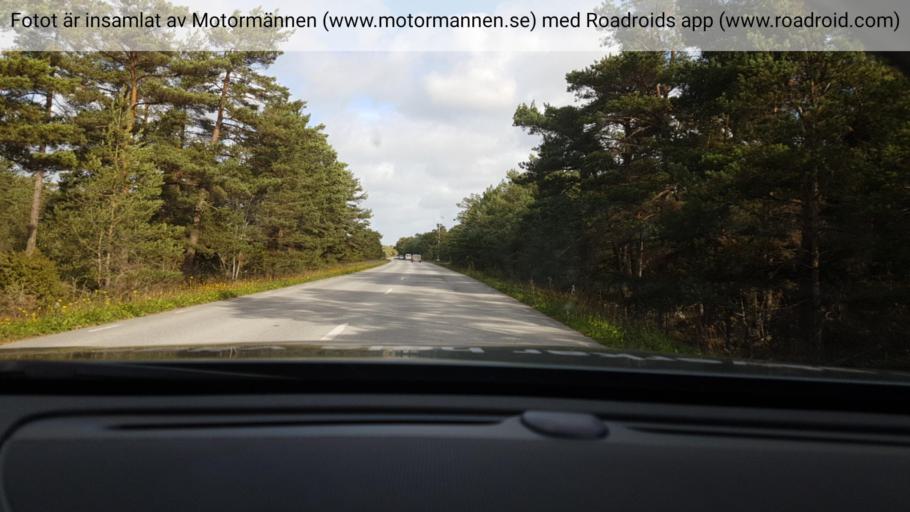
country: SE
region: Gotland
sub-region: Gotland
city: Slite
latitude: 57.8831
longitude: 19.0885
